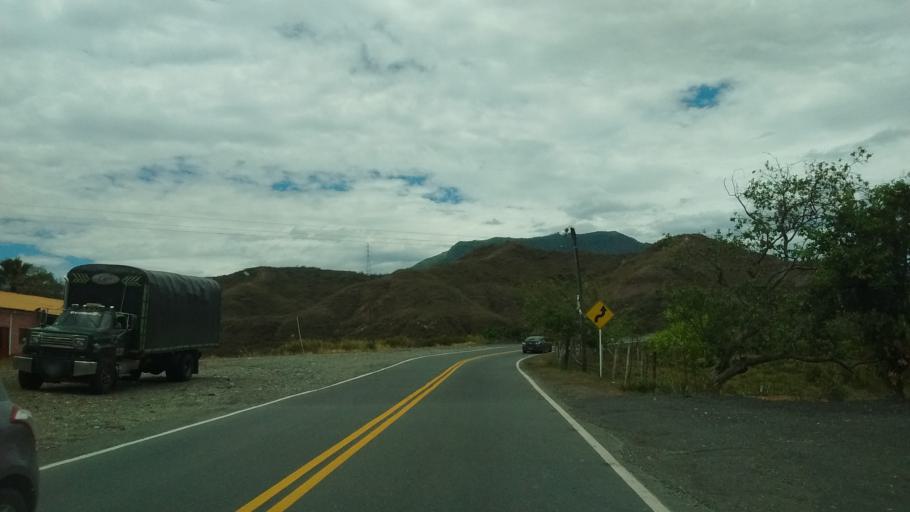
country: CO
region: Cauca
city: La Sierra
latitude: 2.2208
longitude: -76.7987
